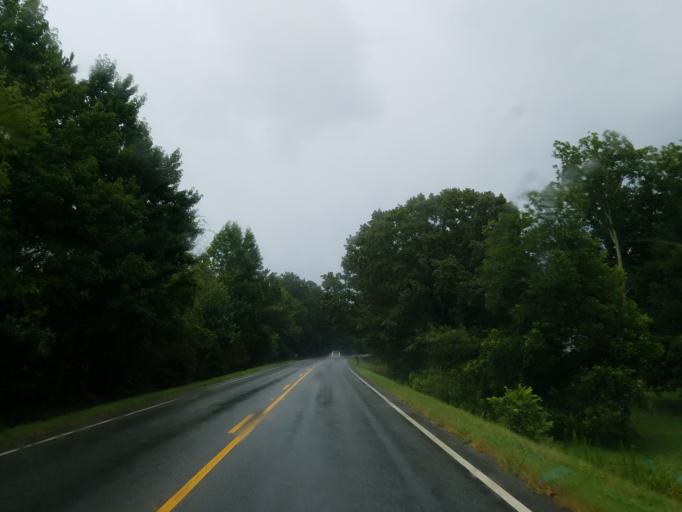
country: US
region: Georgia
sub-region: Floyd County
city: Shannon
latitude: 34.3753
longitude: -85.1058
